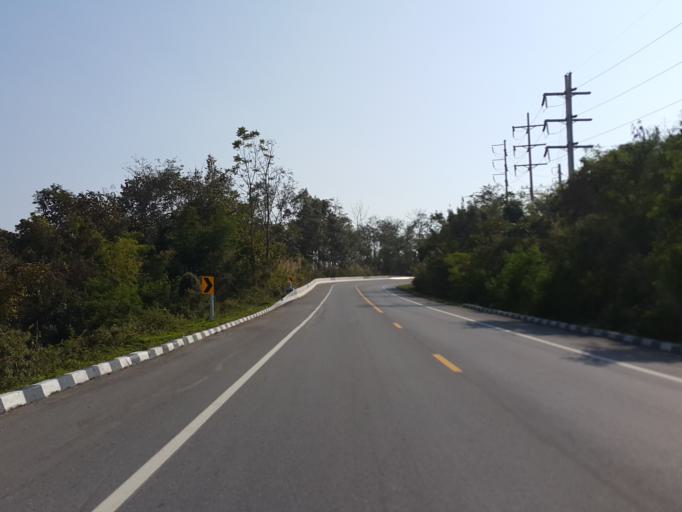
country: TH
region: Lampang
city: Chae Hom
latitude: 18.6030
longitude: 99.5476
